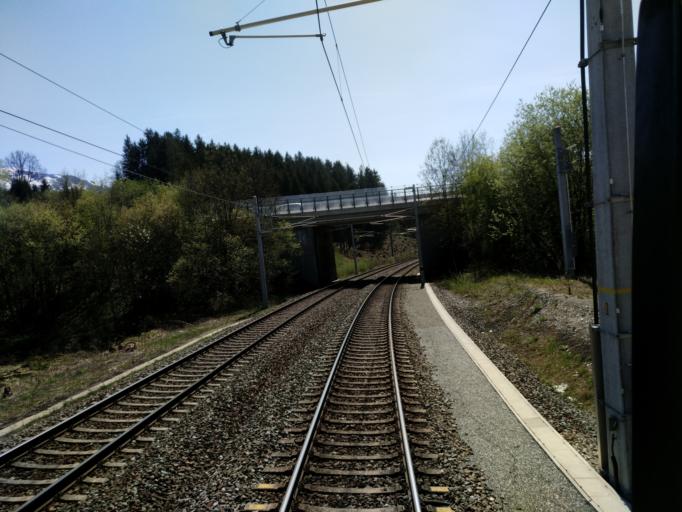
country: AT
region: Salzburg
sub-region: Politischer Bezirk Zell am See
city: Saalfelden am Steinernen Meer
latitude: 47.4202
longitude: 12.8315
